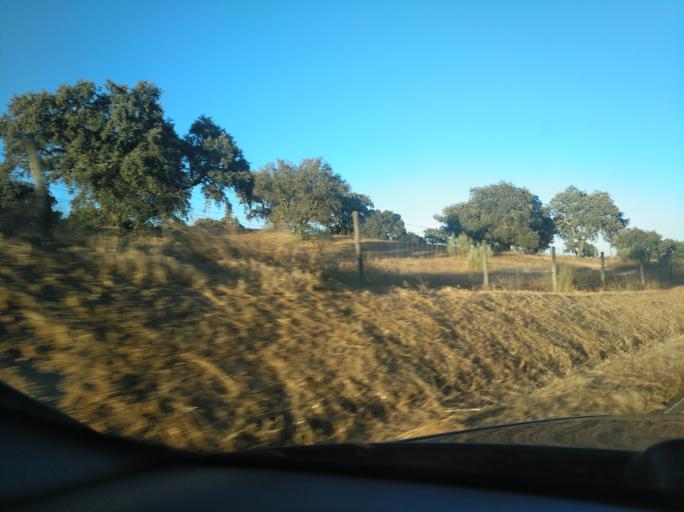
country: PT
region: Portalegre
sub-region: Arronches
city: Arronches
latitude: 39.0684
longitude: -7.2256
